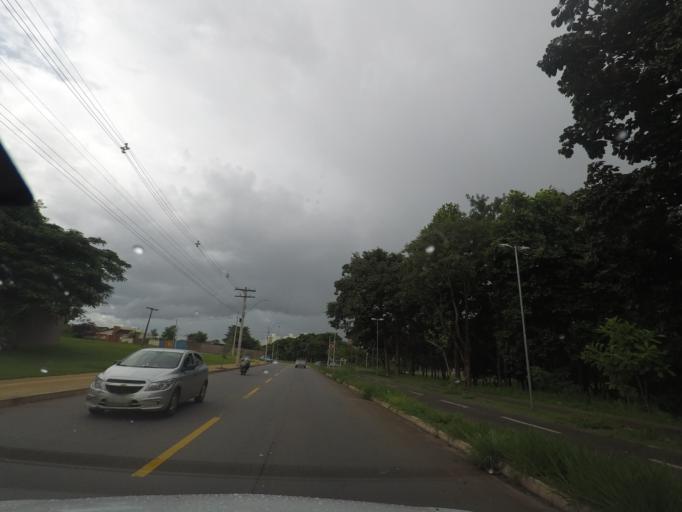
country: BR
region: Goias
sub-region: Goiania
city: Goiania
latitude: -16.7165
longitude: -49.3230
